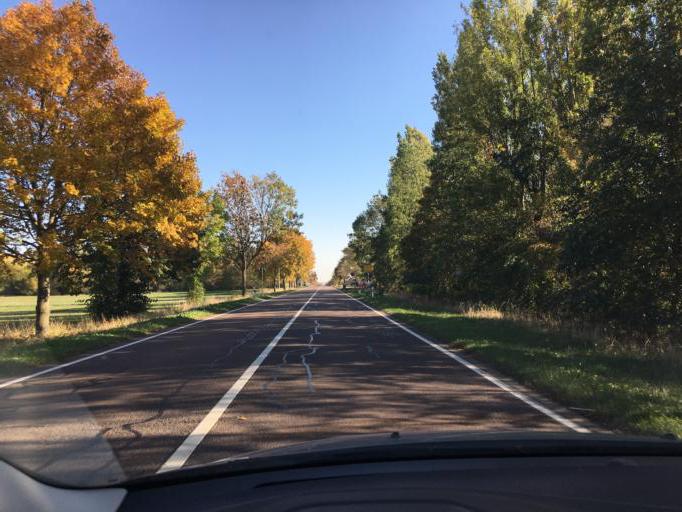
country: DE
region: Saxony-Anhalt
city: Brumby
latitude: 51.8563
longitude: 11.7003
